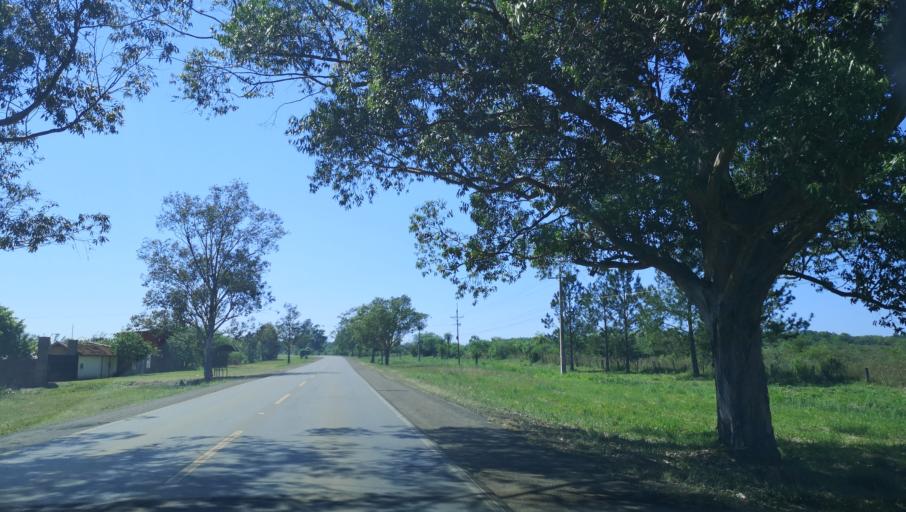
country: PY
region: Itapua
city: Carmen del Parana
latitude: -27.2214
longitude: -56.1224
